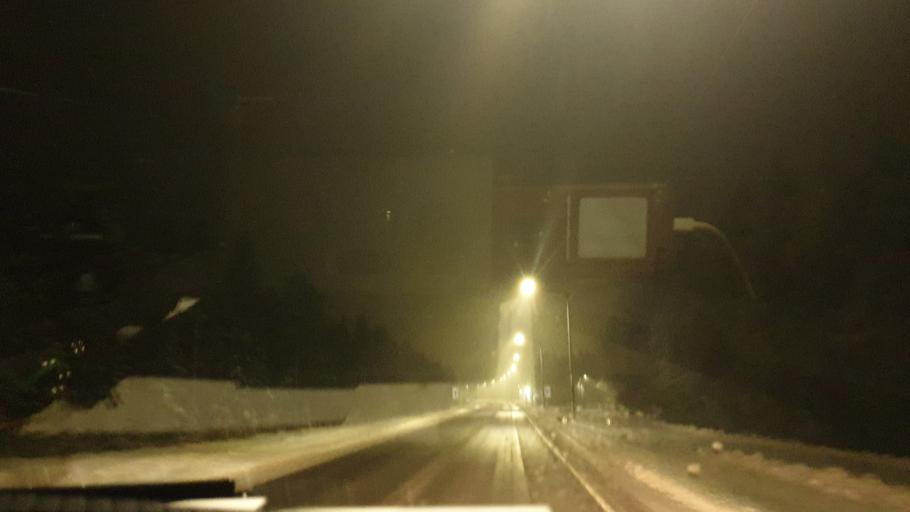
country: FI
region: Northern Ostrobothnia
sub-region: Oulunkaari
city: Kuivaniemi
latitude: 65.5901
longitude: 25.1961
